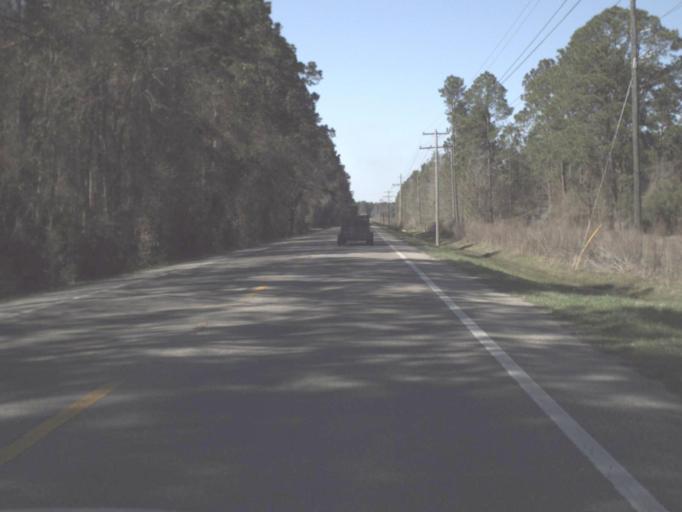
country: US
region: Florida
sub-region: Calhoun County
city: Blountstown
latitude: 30.5187
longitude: -85.1262
